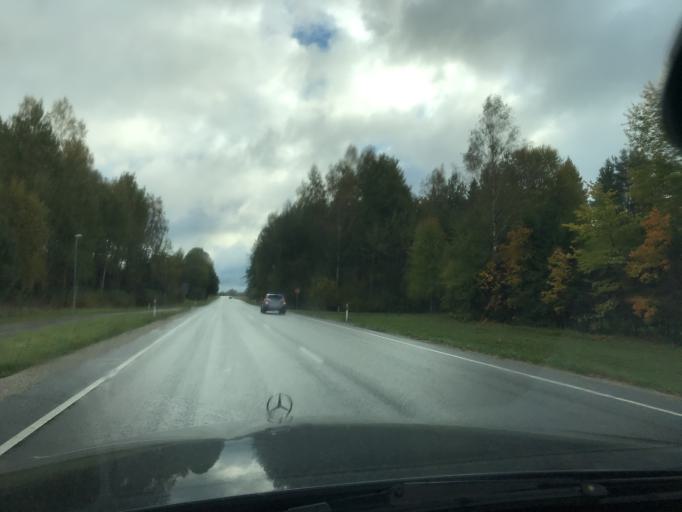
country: EE
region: Viljandimaa
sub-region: Karksi vald
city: Karksi-Nuia
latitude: 58.0105
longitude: 25.7019
